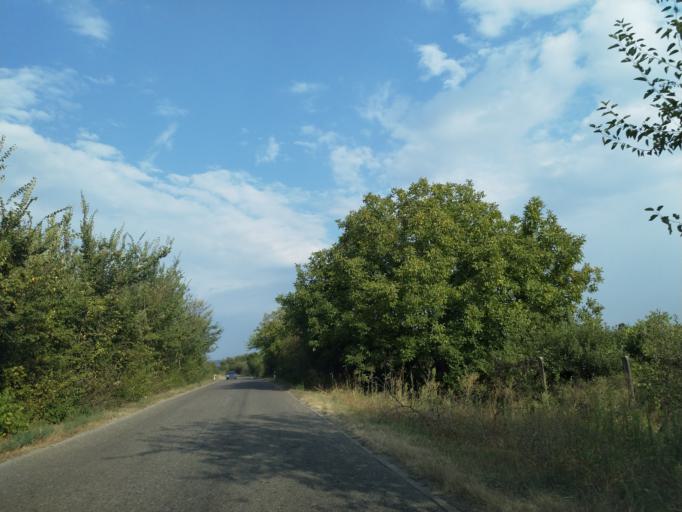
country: RS
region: Central Serbia
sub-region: Pomoravski Okrug
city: Paracin
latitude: 43.8484
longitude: 21.4574
